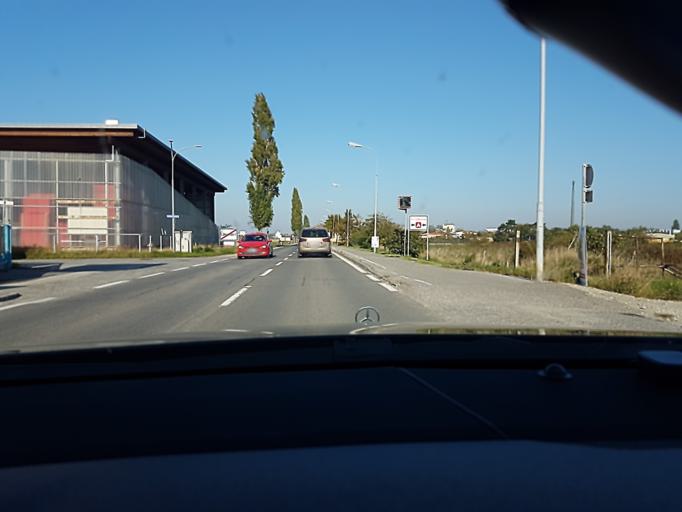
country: AT
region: Lower Austria
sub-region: Politischer Bezirk Wien-Umgebung
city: Lanzendorf
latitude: 48.1148
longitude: 16.4504
